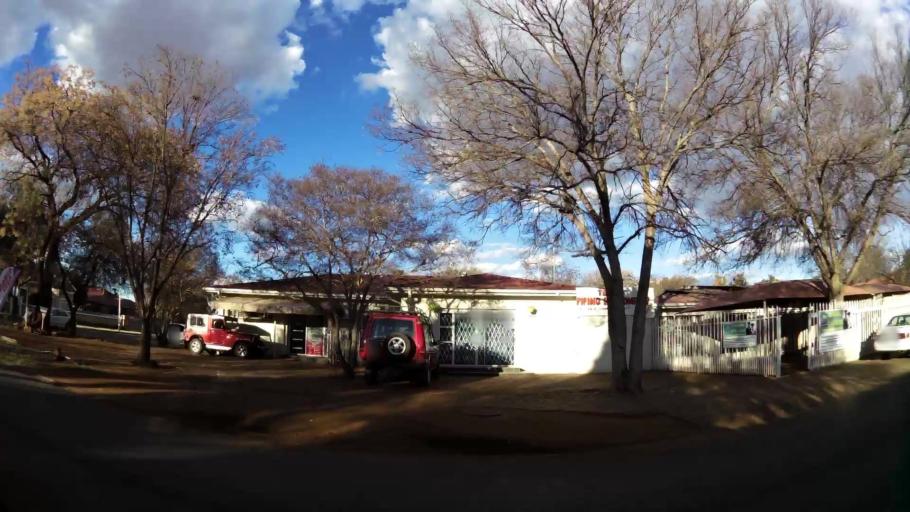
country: ZA
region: North-West
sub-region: Dr Kenneth Kaunda District Municipality
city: Potchefstroom
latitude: -26.7076
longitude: 27.0997
